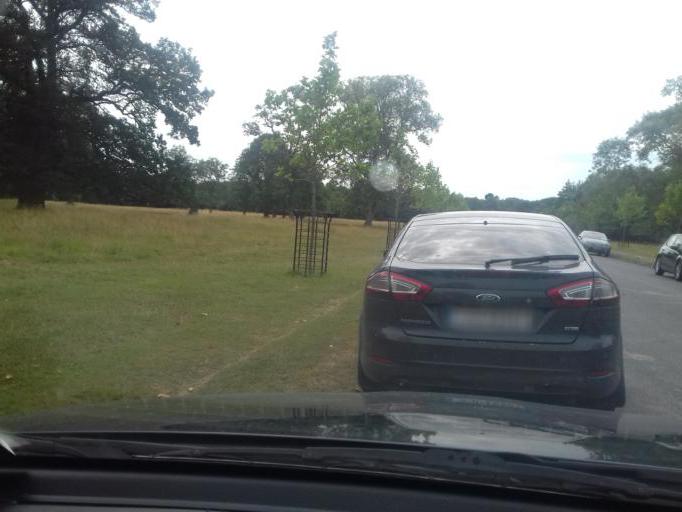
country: IE
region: Leinster
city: Chapelizod
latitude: 53.3602
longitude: -6.3454
